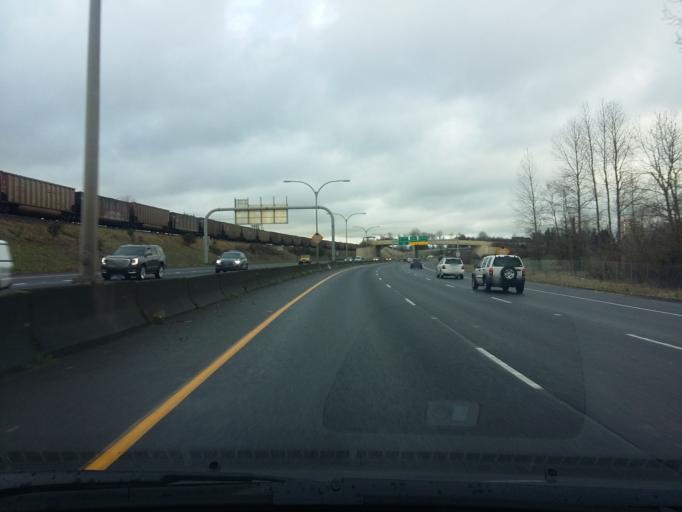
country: US
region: Washington
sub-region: Clark County
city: Vancouver
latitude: 45.6196
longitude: -122.6632
